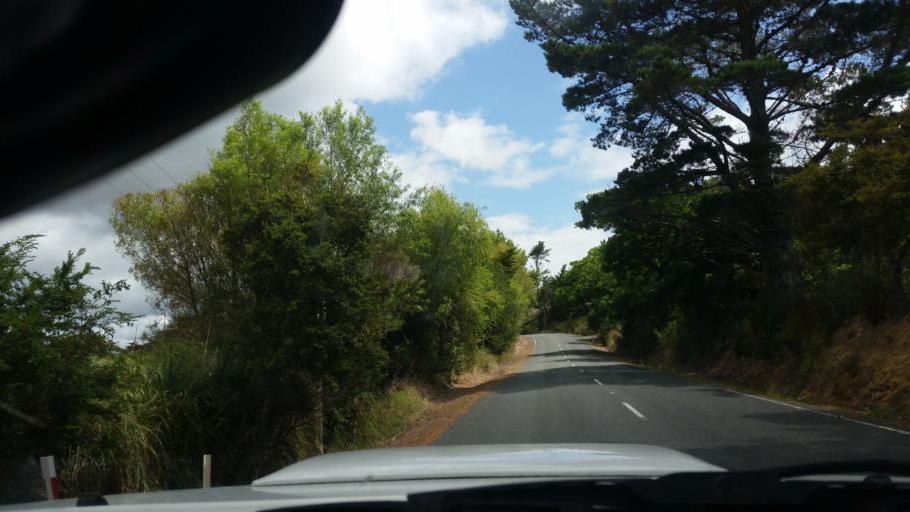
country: NZ
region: Auckland
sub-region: Auckland
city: Wellsford
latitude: -36.1430
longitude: 174.5577
